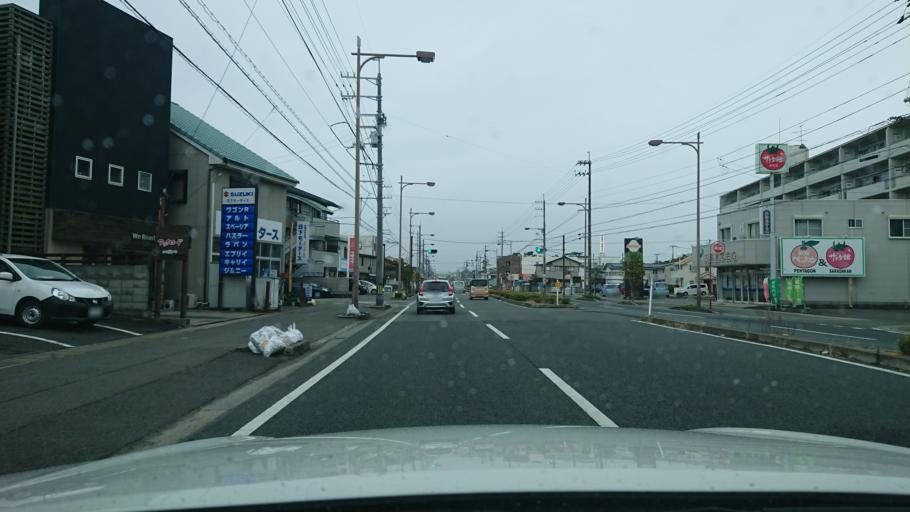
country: JP
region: Tokushima
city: Tokushima-shi
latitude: 34.0866
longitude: 134.5381
